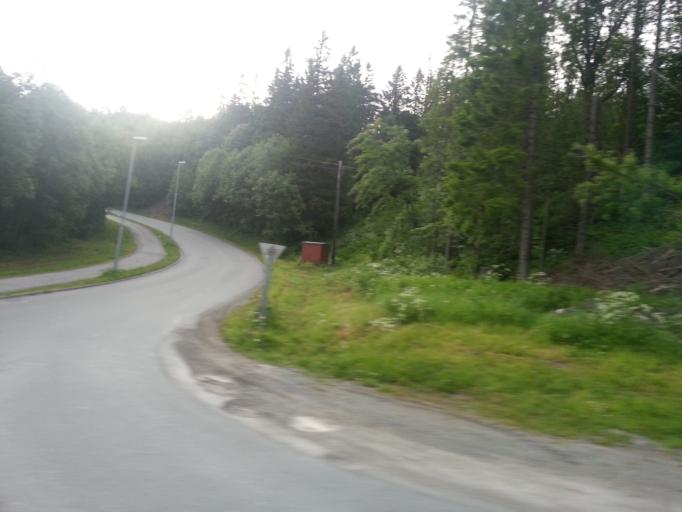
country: NO
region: Sor-Trondelag
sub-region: Malvik
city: Malvik
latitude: 63.4301
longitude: 10.6290
